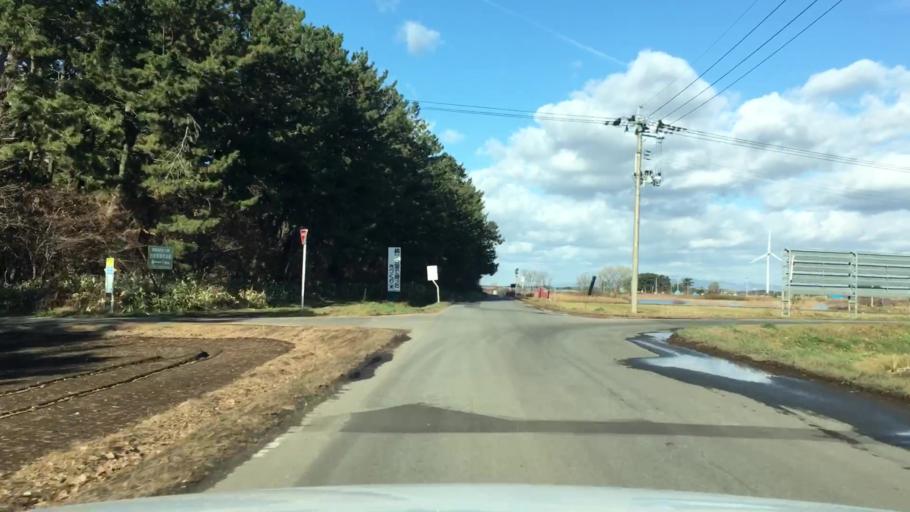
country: JP
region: Aomori
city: Shimokizukuri
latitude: 40.8489
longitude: 140.2999
